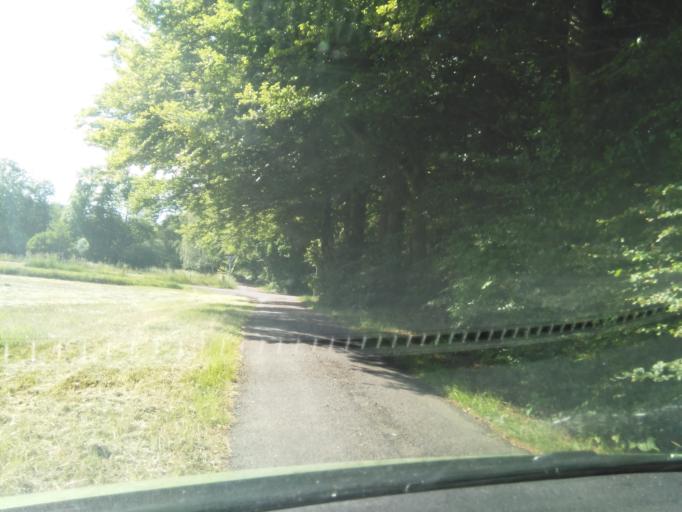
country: DK
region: Capital Region
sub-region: Bornholm Kommune
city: Nexo
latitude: 55.0864
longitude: 15.0651
